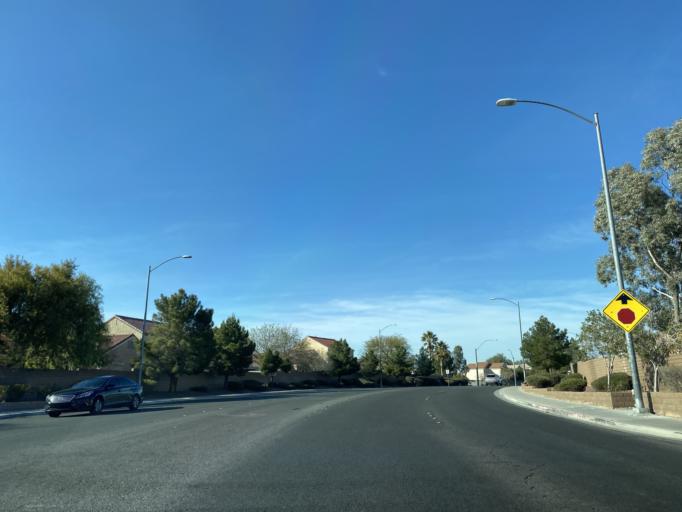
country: US
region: Nevada
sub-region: Clark County
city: Summerlin South
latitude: 36.3051
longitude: -115.2873
